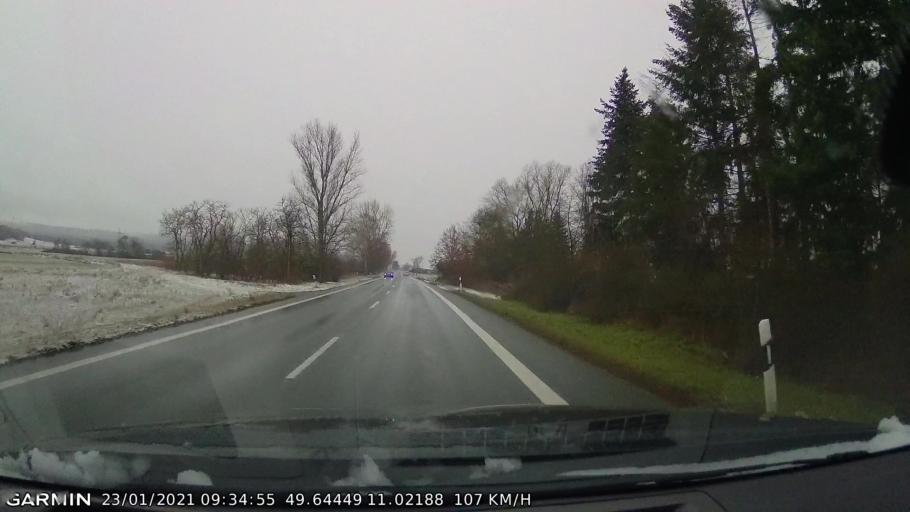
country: DE
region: Bavaria
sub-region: Regierungsbezirk Mittelfranken
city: Bubenreuth
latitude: 49.6440
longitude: 11.0219
